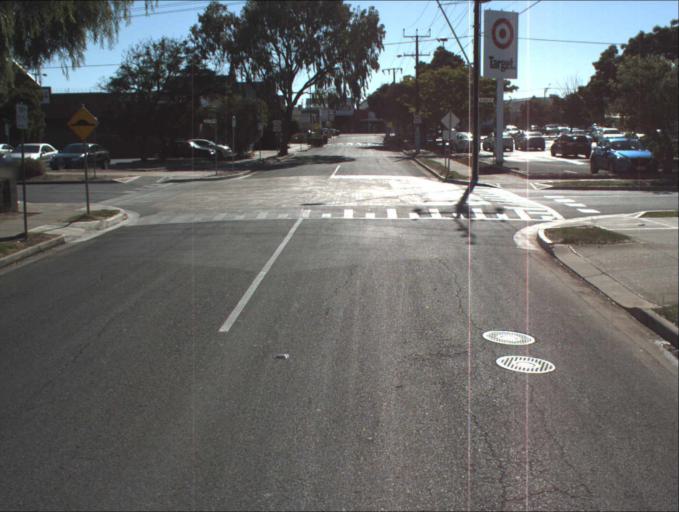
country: AU
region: South Australia
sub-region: Prospect
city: Prospect
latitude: -34.8754
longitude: 138.6041
